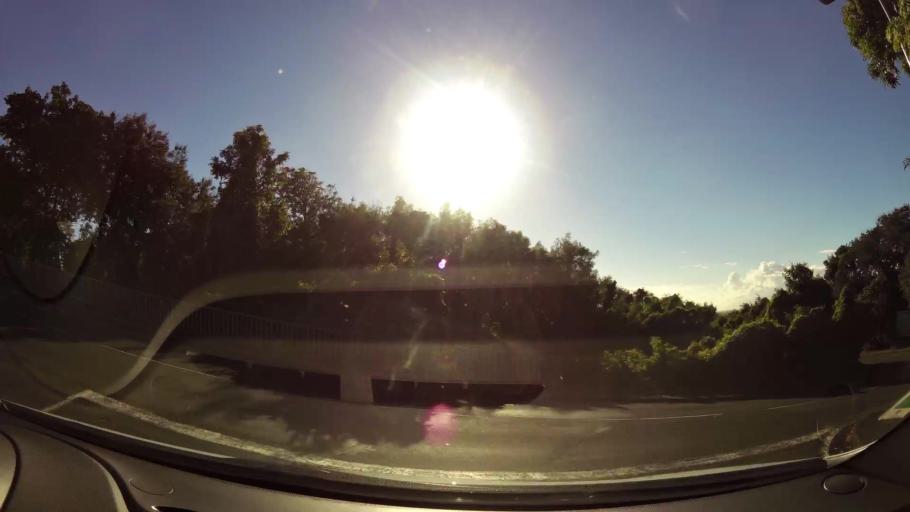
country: RE
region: Reunion
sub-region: Reunion
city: Saint-Denis
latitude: -20.8943
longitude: 55.4514
